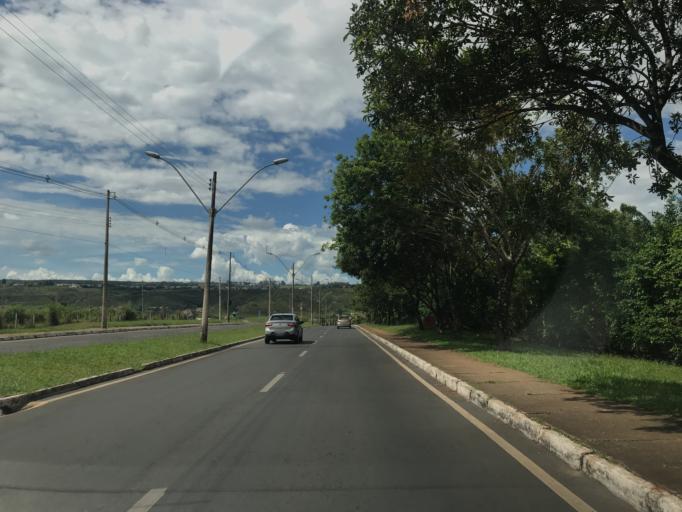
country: BR
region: Federal District
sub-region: Brasilia
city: Brasilia
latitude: -15.7209
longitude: -47.8807
